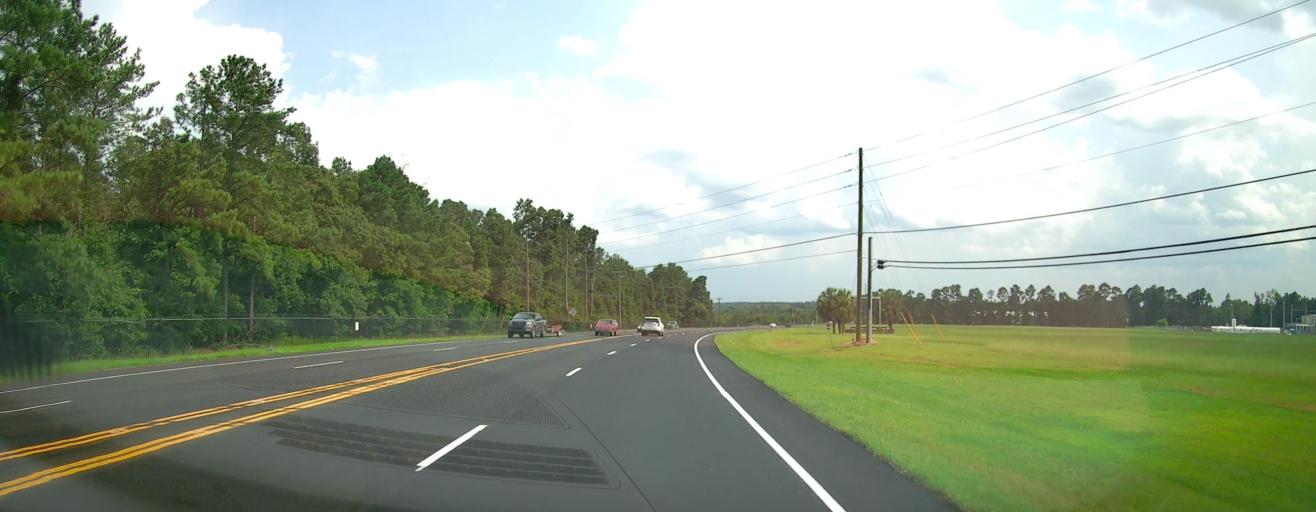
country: US
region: Georgia
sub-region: Houston County
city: Robins Air Force Base
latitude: 32.5889
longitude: -83.5885
